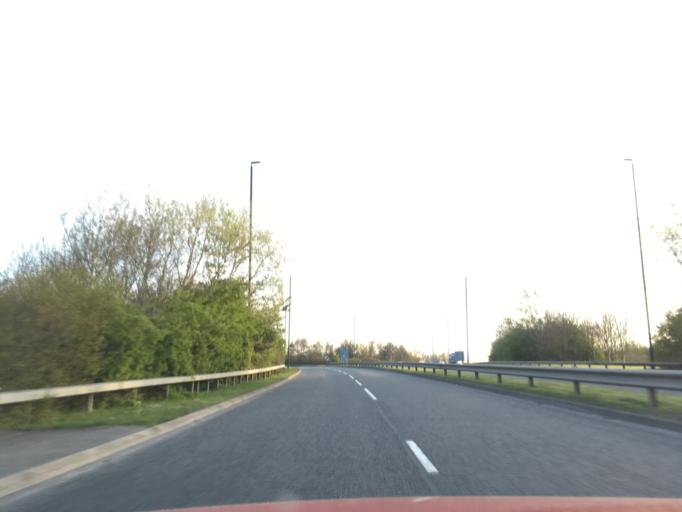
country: GB
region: England
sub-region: Gloucestershire
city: Churchdown
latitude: 51.8551
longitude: -2.1694
